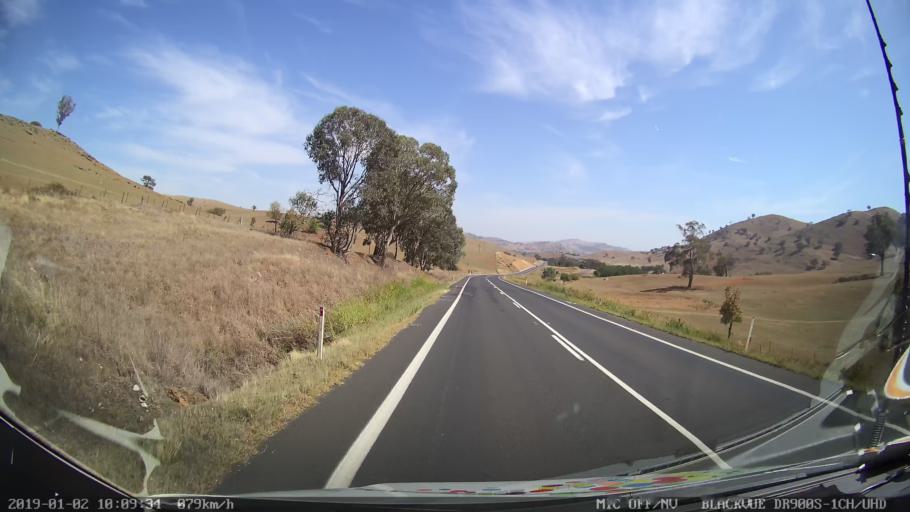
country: AU
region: New South Wales
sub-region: Gundagai
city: Gundagai
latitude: -35.1155
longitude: 148.0983
